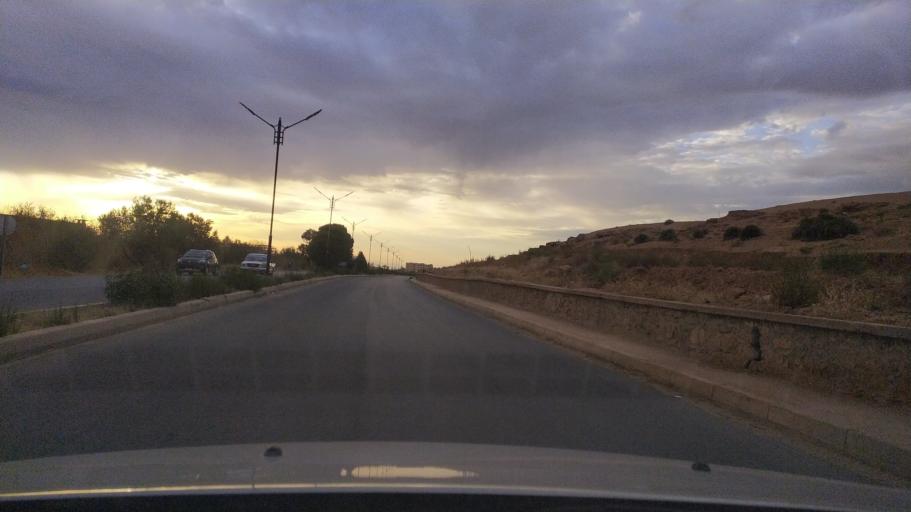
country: DZ
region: Tiaret
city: Frenda
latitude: 35.0514
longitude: 1.0715
